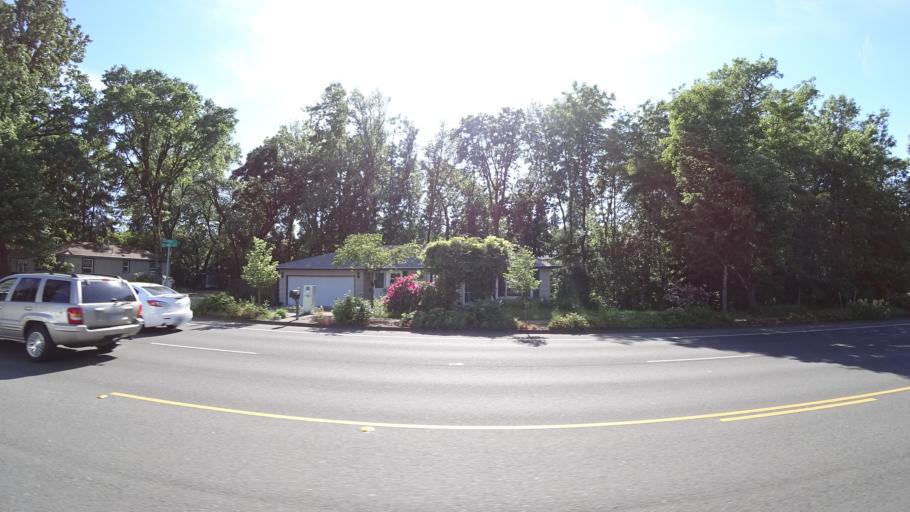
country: US
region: Oregon
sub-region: Washington County
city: Beaverton
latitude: 45.4716
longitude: -122.8050
